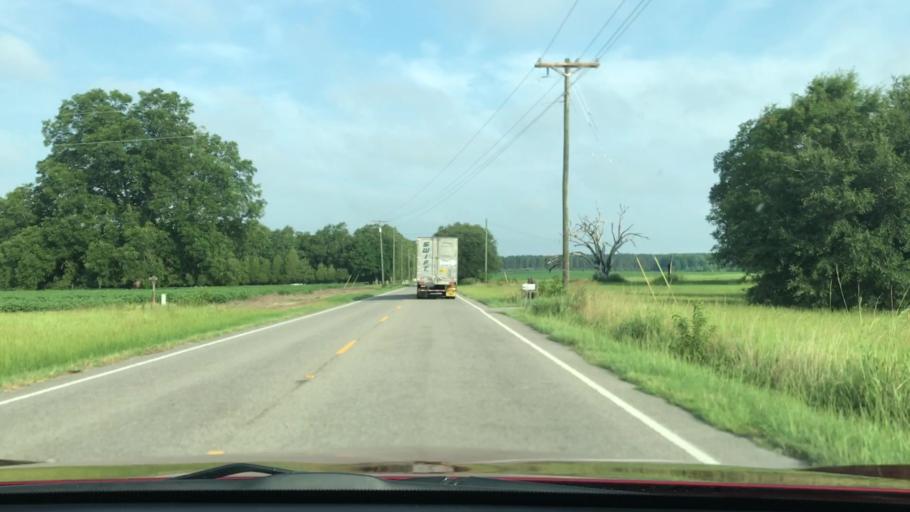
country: US
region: South Carolina
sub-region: Barnwell County
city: Blackville
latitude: 33.6088
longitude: -81.2724
